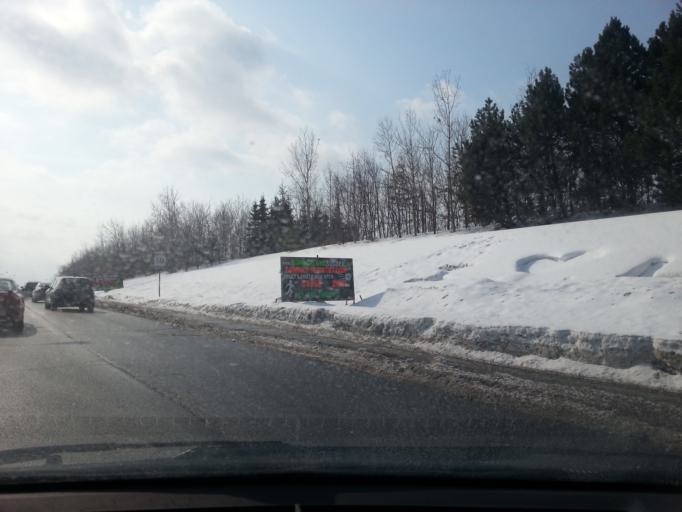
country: CA
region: Quebec
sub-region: Outaouais
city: Gatineau
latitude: 45.4808
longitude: -75.4991
